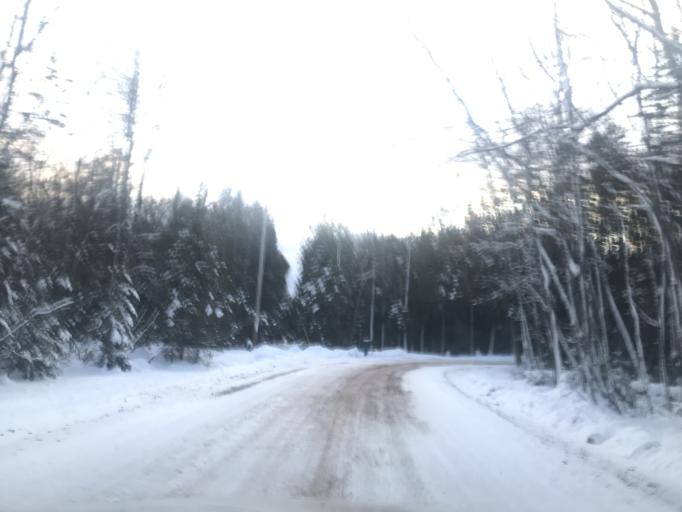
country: US
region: Michigan
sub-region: Menominee County
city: Menominee
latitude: 45.4195
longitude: -87.3354
